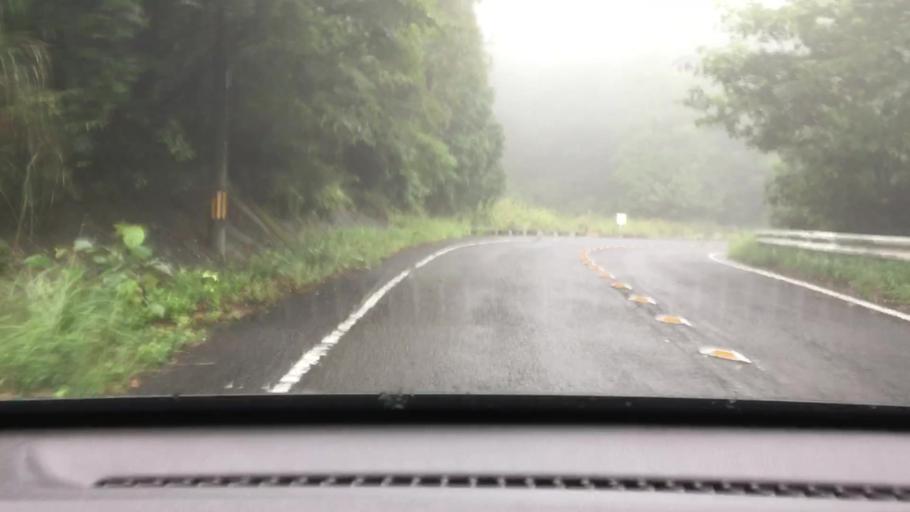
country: JP
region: Nagasaki
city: Togitsu
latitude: 32.9519
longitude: 129.7409
